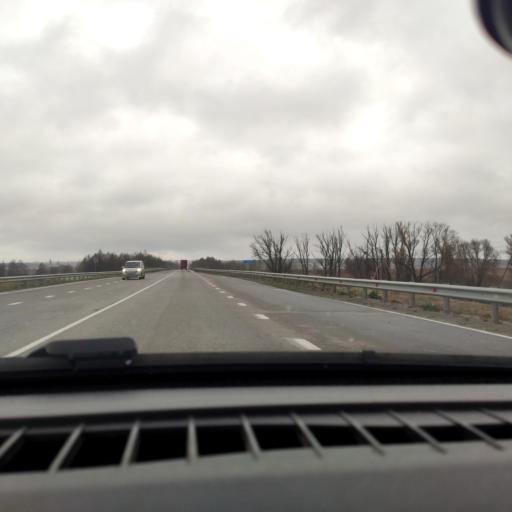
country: RU
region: Voronezj
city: Ostrogozhsk
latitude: 51.0301
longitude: 38.9866
